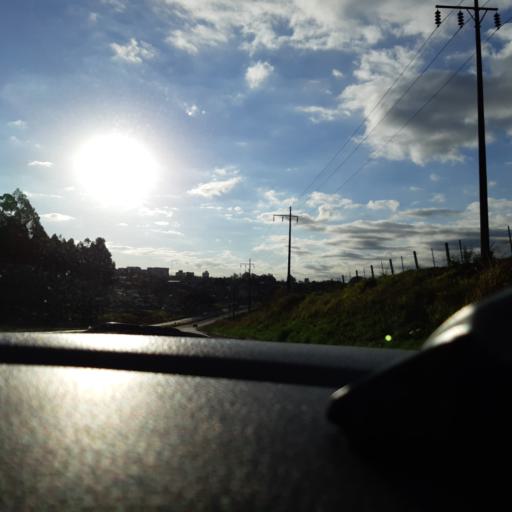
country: BR
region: Sao Paulo
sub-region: Ourinhos
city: Ourinhos
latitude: -22.9907
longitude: -49.8513
